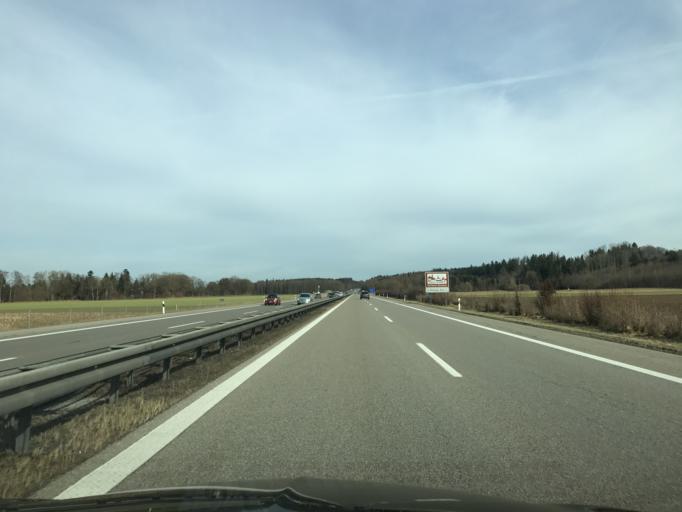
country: DE
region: Bavaria
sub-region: Swabia
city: Buxheim
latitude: 47.9651
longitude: 10.1132
